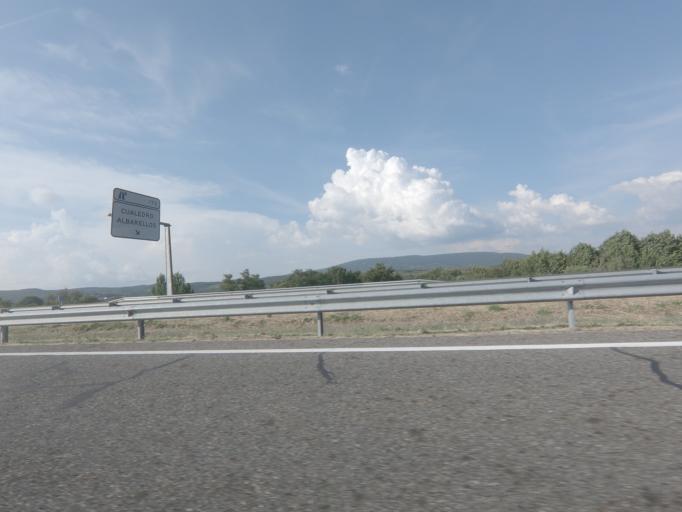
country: ES
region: Galicia
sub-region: Provincia de Ourense
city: Cualedro
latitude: 41.9778
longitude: -7.5357
